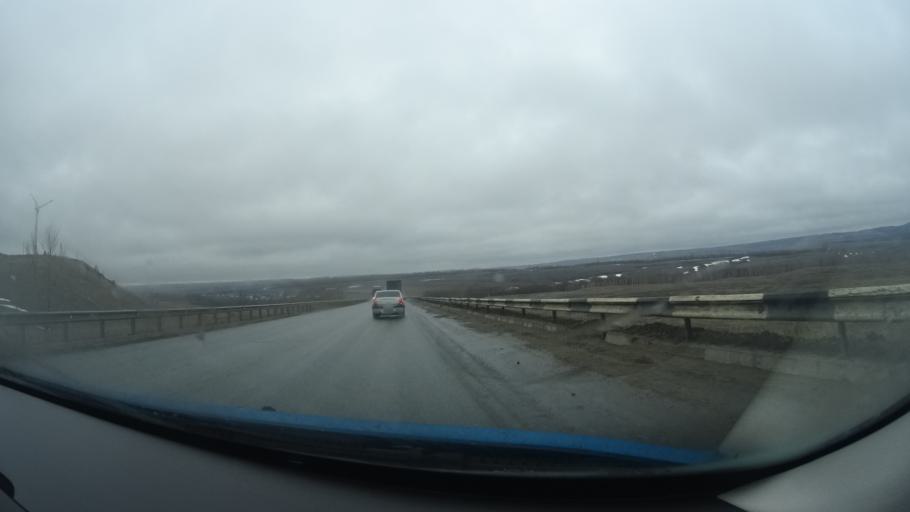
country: RU
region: Bashkortostan
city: Kandry
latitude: 54.5814
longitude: 54.2459
